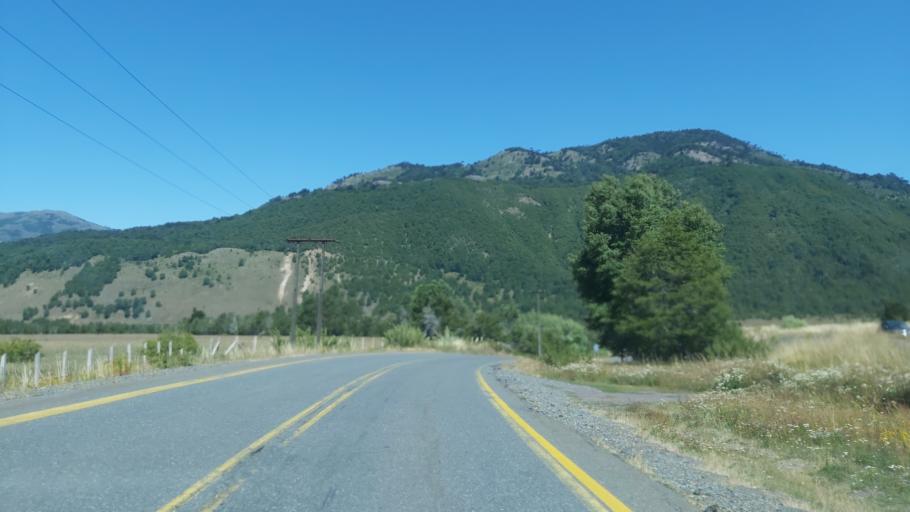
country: CL
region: Araucania
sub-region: Provincia de Cautin
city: Vilcun
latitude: -38.5613
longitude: -71.4943
